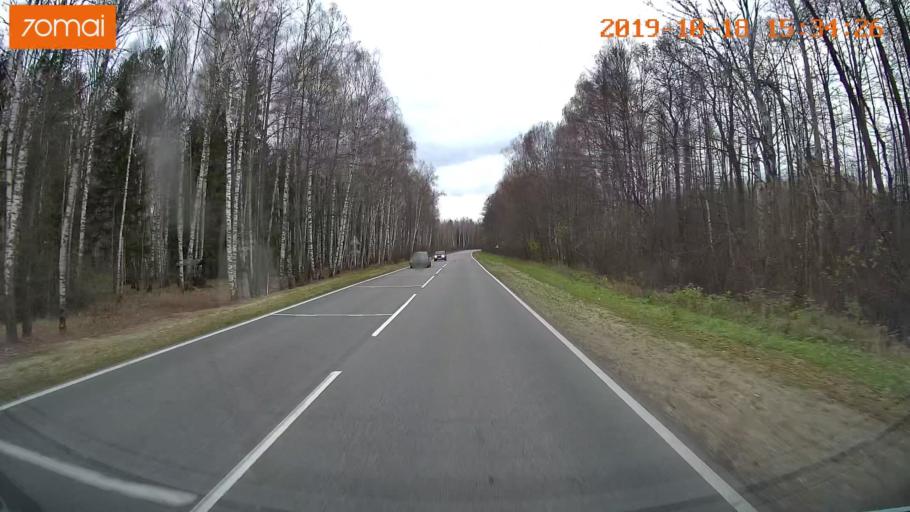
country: RU
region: Vladimir
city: Anopino
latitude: 55.8542
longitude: 40.6427
